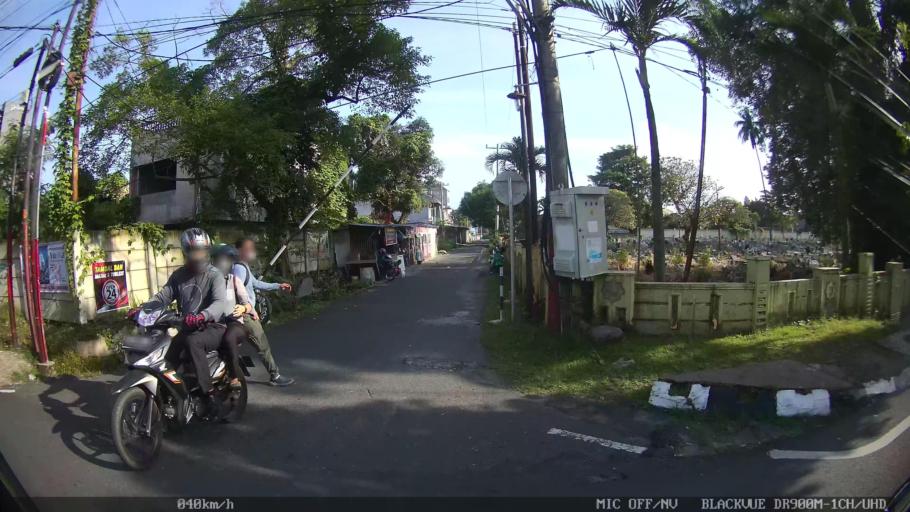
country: ID
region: North Sumatra
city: Medan
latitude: 3.5937
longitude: 98.6697
